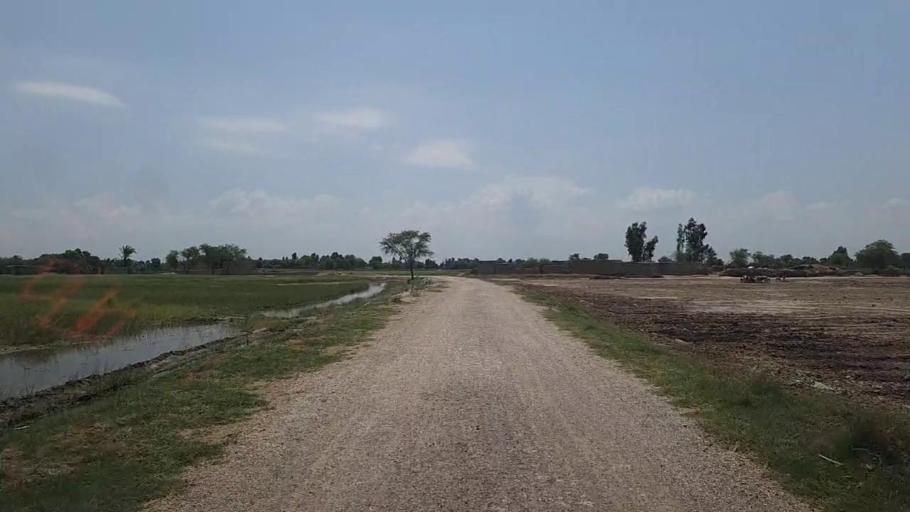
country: PK
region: Sindh
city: Ubauro
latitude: 28.1540
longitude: 69.7656
